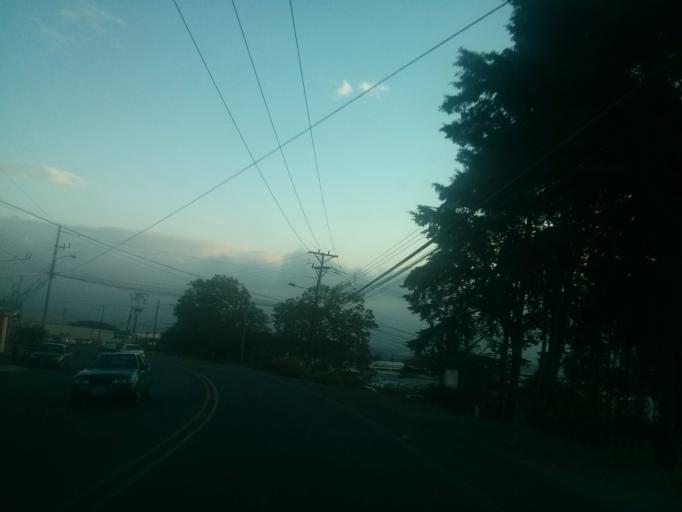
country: CR
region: Cartago
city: Cartago
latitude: 9.8813
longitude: -83.9220
